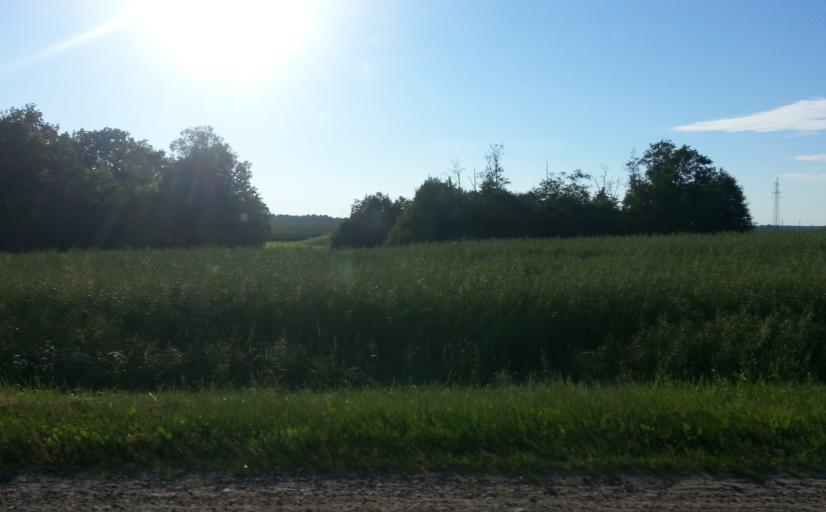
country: LT
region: Panevezys
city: Pasvalys
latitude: 56.1099
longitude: 24.4657
